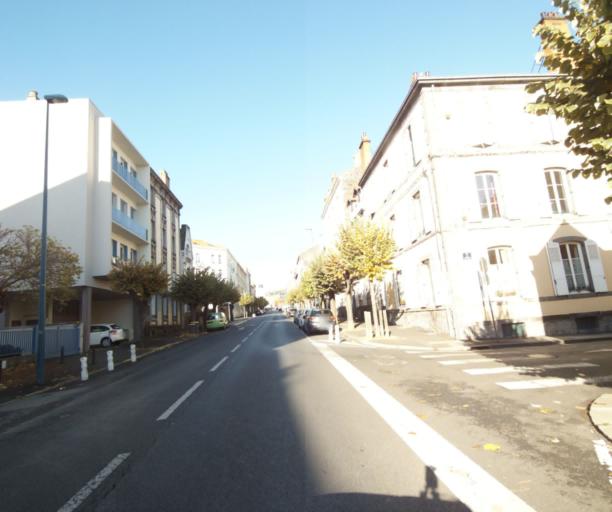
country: FR
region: Auvergne
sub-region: Departement du Puy-de-Dome
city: Clermont-Ferrand
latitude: 45.7782
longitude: 3.0942
